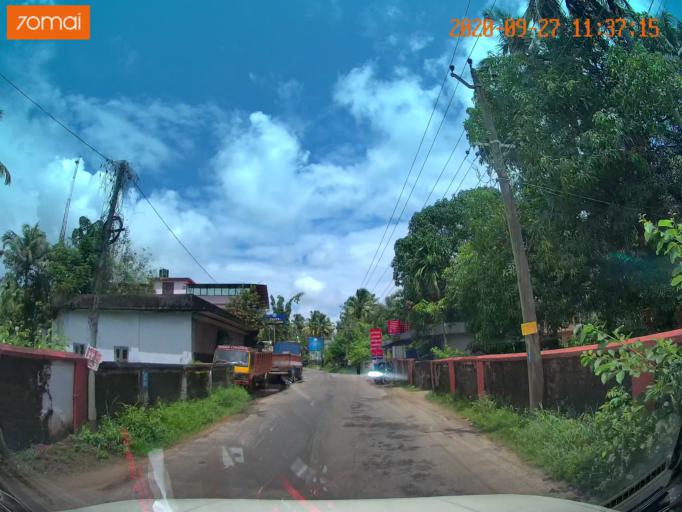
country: IN
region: Kerala
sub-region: Thrissur District
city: Thanniyam
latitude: 10.4539
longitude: 76.1236
